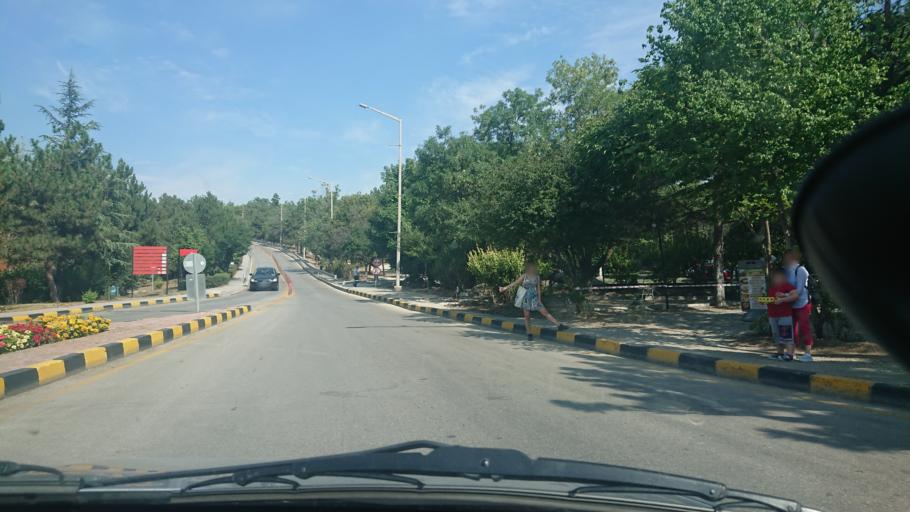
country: TR
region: Ankara
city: Ankara
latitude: 39.8900
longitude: 32.7904
